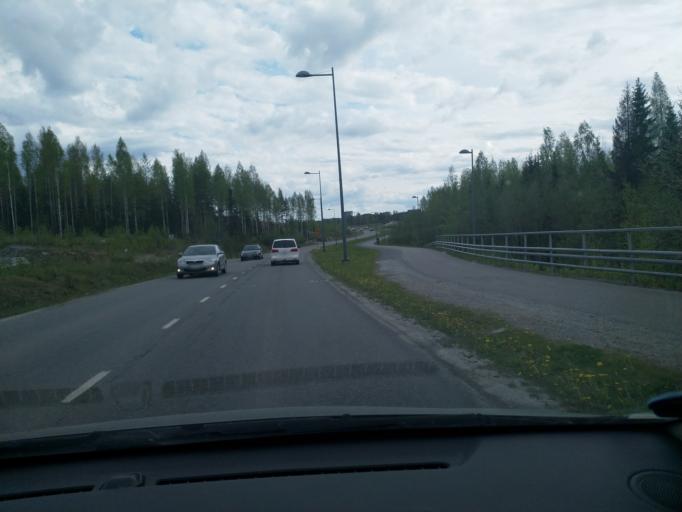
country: FI
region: Pirkanmaa
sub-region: Tampere
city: Tampere
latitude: 61.4473
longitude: 23.8065
